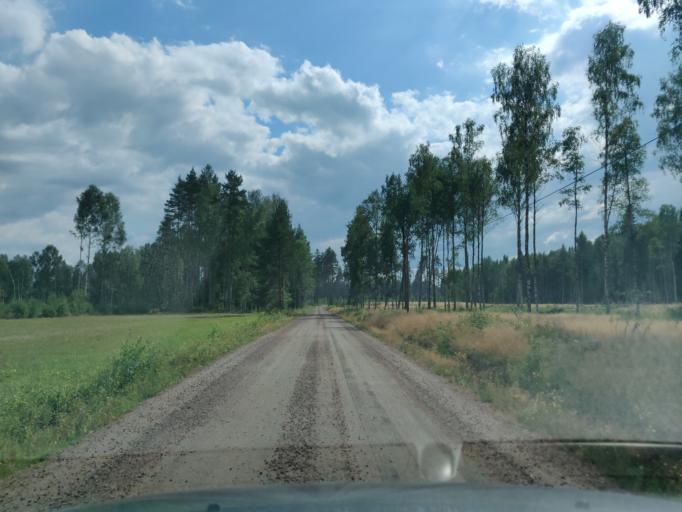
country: SE
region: Vaermland
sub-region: Hagfors Kommun
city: Hagfors
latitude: 59.9921
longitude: 13.5662
